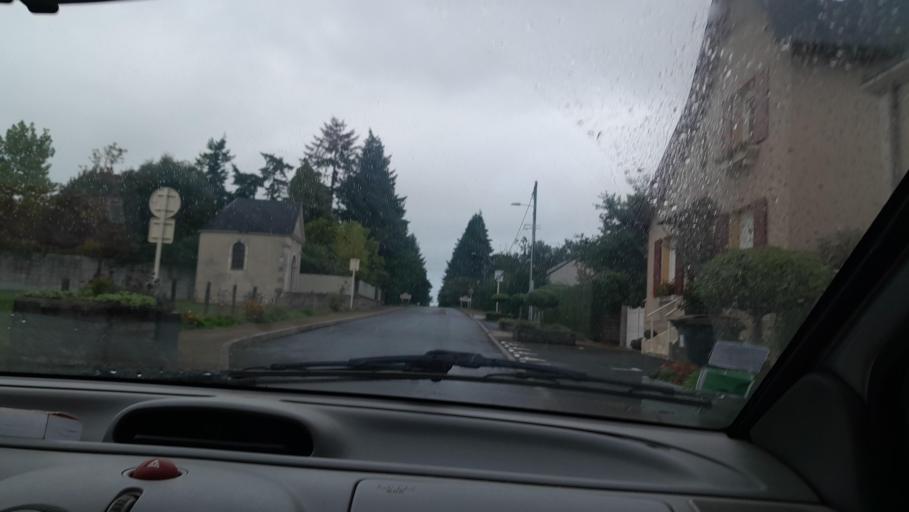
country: FR
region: Pays de la Loire
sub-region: Departement de la Mayenne
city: Congrier
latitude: 47.8807
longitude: -1.1264
